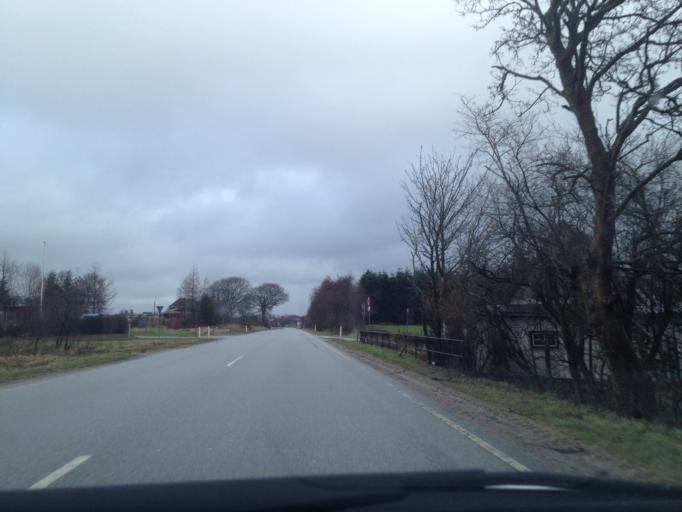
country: DK
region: South Denmark
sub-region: Kolding Kommune
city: Vamdrup
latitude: 55.3607
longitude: 9.1980
